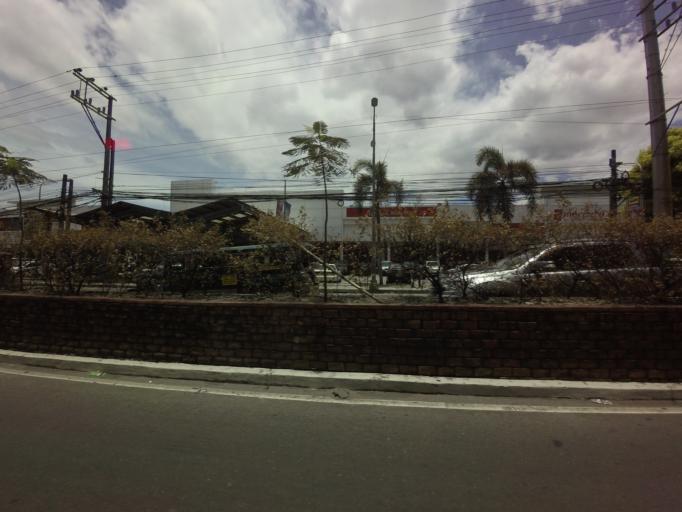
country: PH
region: Metro Manila
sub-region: Marikina
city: Calumpang
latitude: 14.6195
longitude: 121.1018
